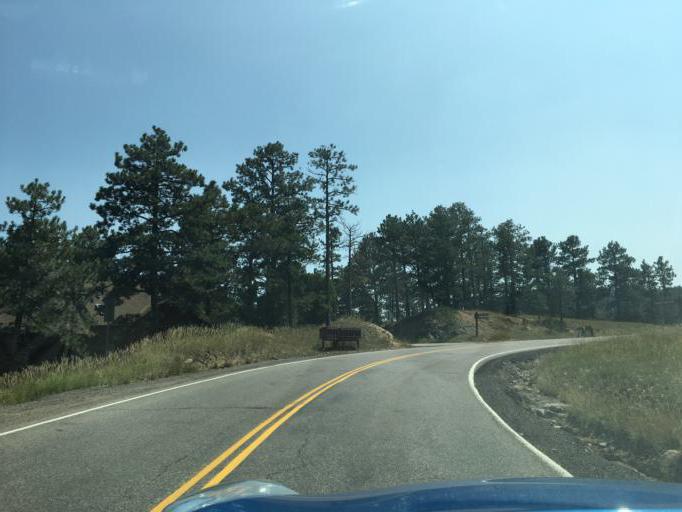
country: US
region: Colorado
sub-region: Jefferson County
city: Genesee
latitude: 39.6959
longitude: -105.2669
